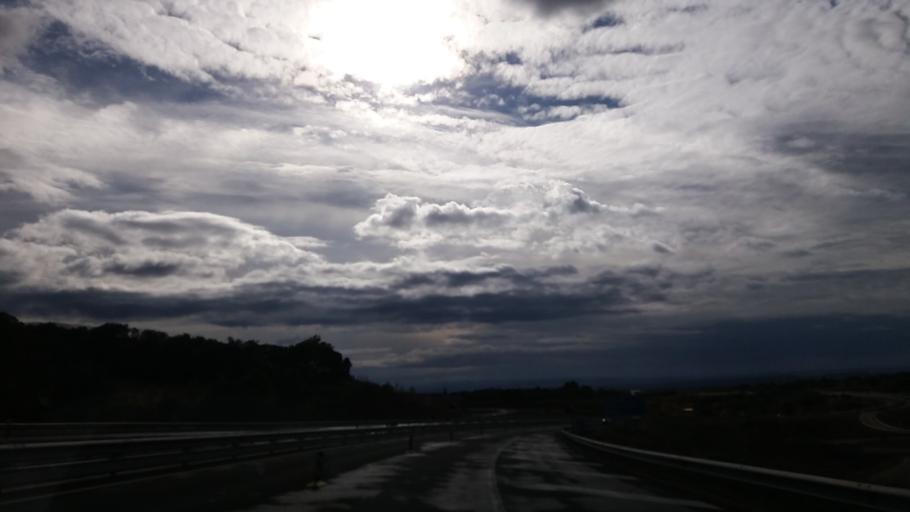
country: ES
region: Aragon
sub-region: Provincia de Huesca
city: Nueno
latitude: 42.2671
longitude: -0.4345
